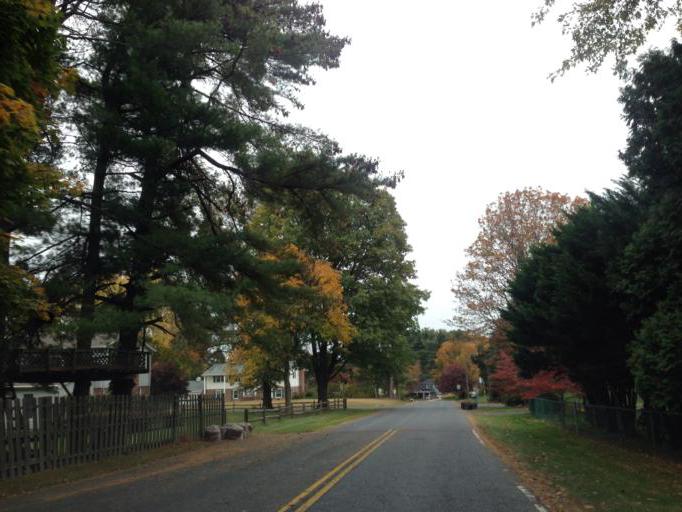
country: US
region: Maryland
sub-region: Howard County
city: Ellicott City
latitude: 39.3017
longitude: -76.8316
